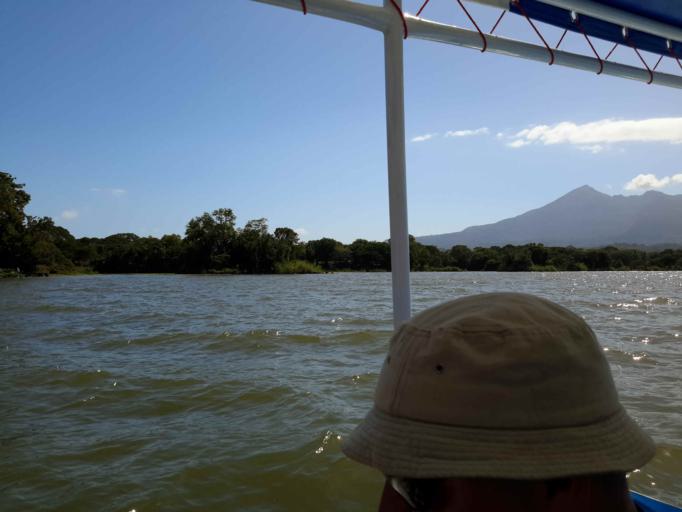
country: NI
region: Granada
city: Granada
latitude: 11.9184
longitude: -85.9247
